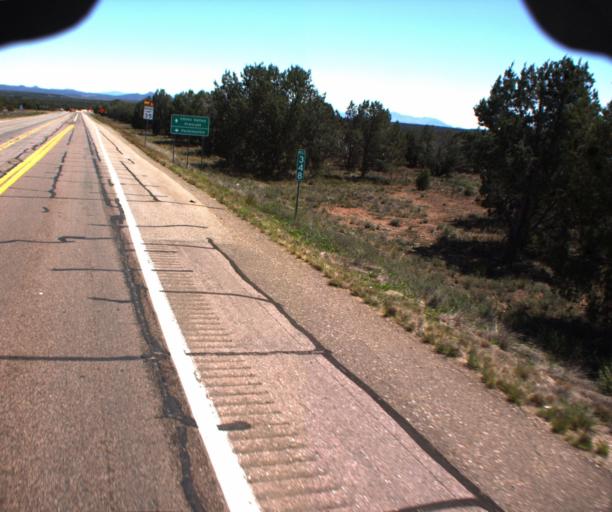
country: US
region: Arizona
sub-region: Yavapai County
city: Paulden
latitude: 35.0071
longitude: -112.3902
